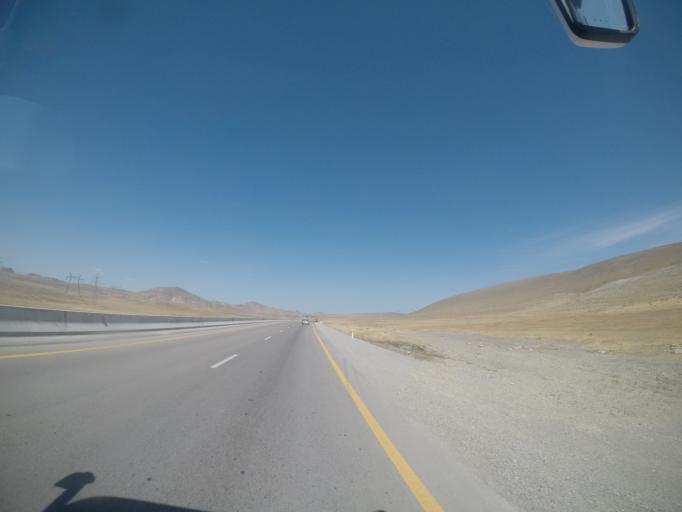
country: AZ
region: Sumqayit
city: Haci Zeynalabdin
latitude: 40.4950
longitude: 49.3229
